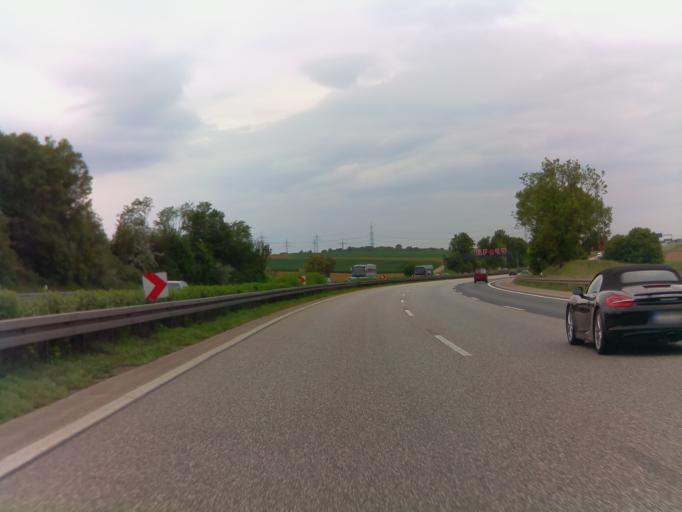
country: DE
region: Hesse
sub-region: Regierungsbezirk Darmstadt
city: Butzbach
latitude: 50.4469
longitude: 8.6970
